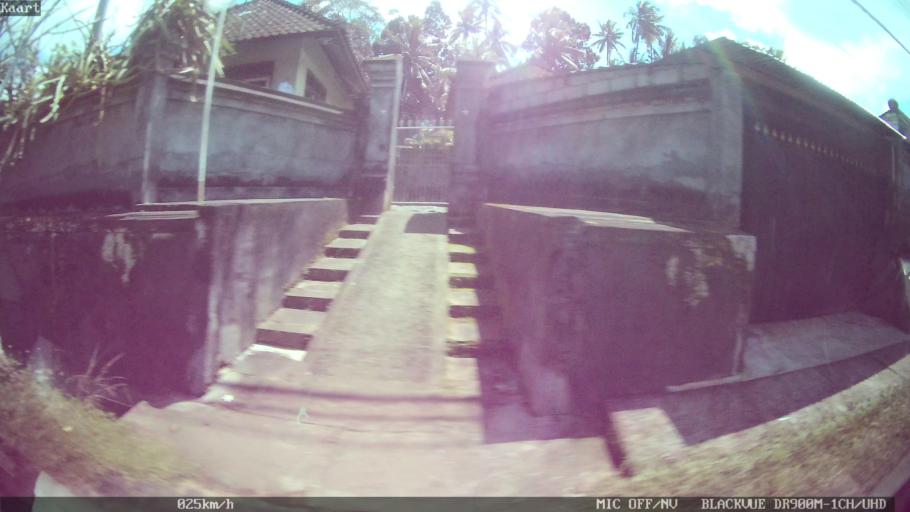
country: ID
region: Bali
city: Banjar Kelodan
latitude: -8.5135
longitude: 115.3346
